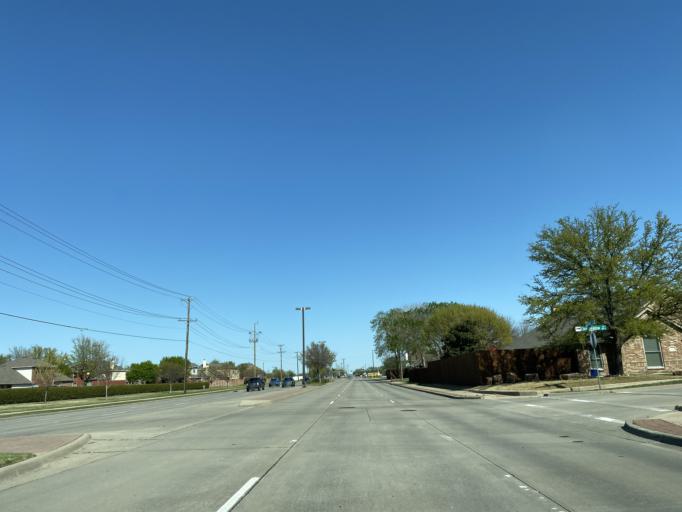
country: US
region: Texas
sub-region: Collin County
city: Allen
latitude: 33.1001
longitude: -96.6262
